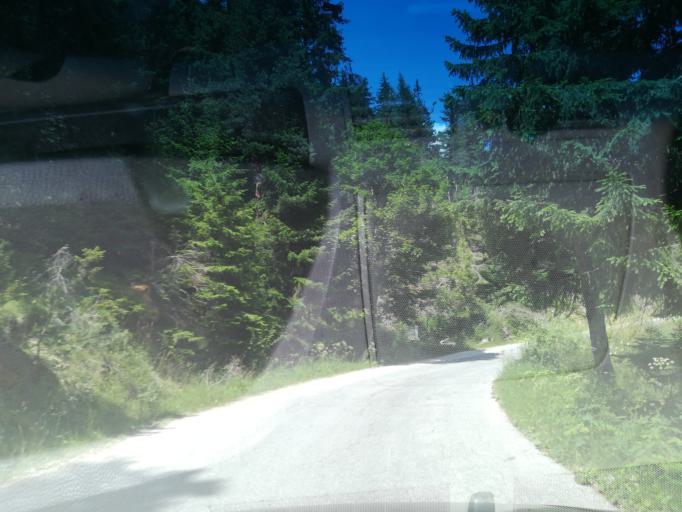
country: BG
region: Smolyan
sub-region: Obshtina Chepelare
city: Chepelare
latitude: 41.6882
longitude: 24.7715
